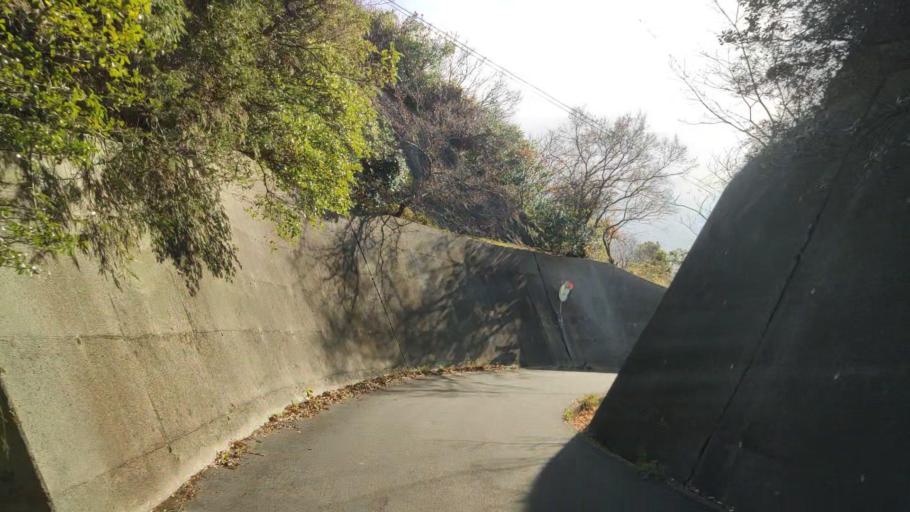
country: JP
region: Hiroshima
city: Innoshima
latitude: 34.2129
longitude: 133.1278
